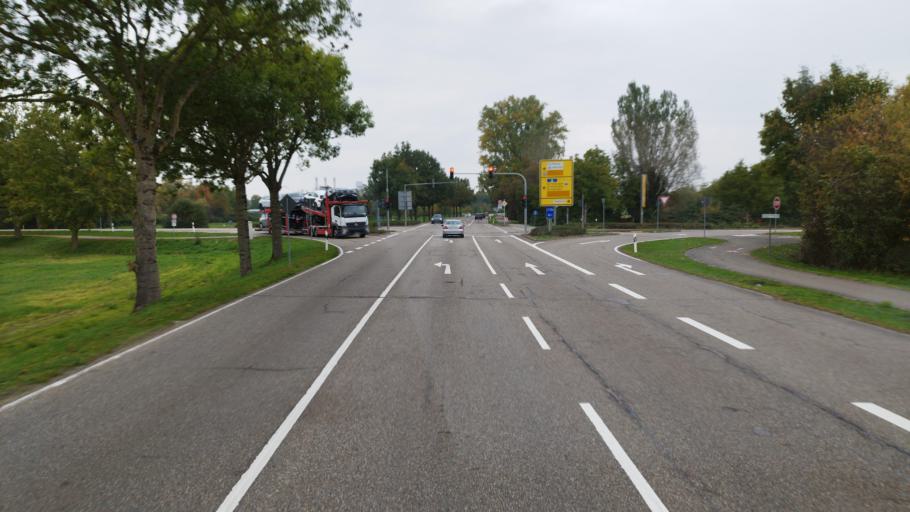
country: DE
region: Baden-Wuerttemberg
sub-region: Karlsruhe Region
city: Rheinau
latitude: 48.8535
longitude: 8.1912
